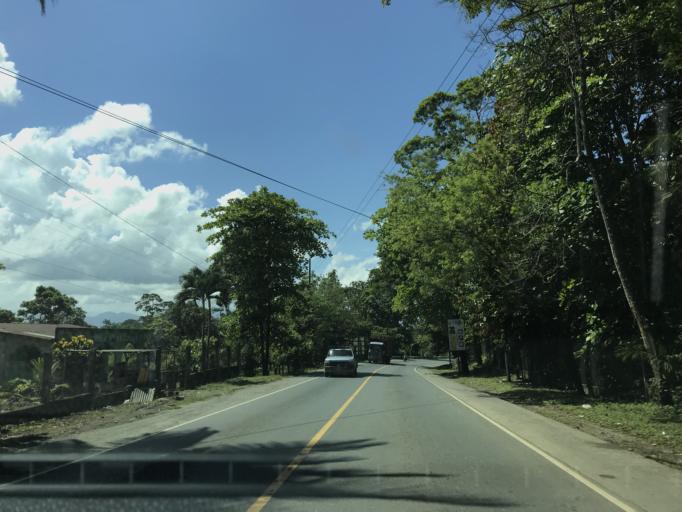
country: GT
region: Izabal
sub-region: Municipio de Puerto Barrios
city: Puerto Barrios
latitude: 15.6581
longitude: -88.5501
